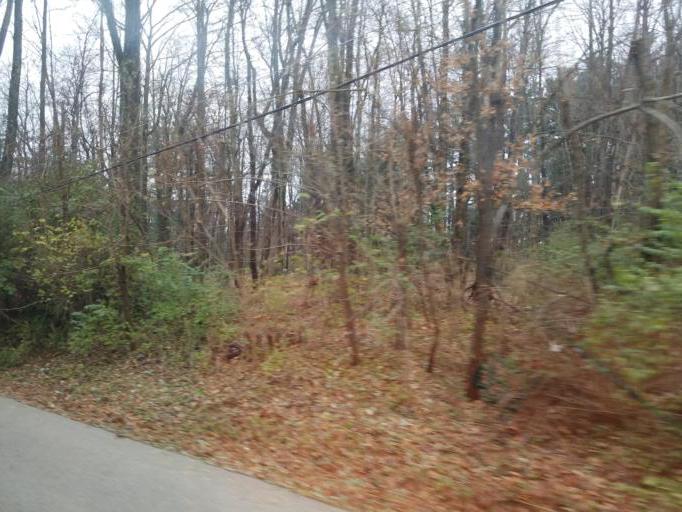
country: US
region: Ohio
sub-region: Richland County
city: Mansfield
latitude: 40.7193
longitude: -82.5342
